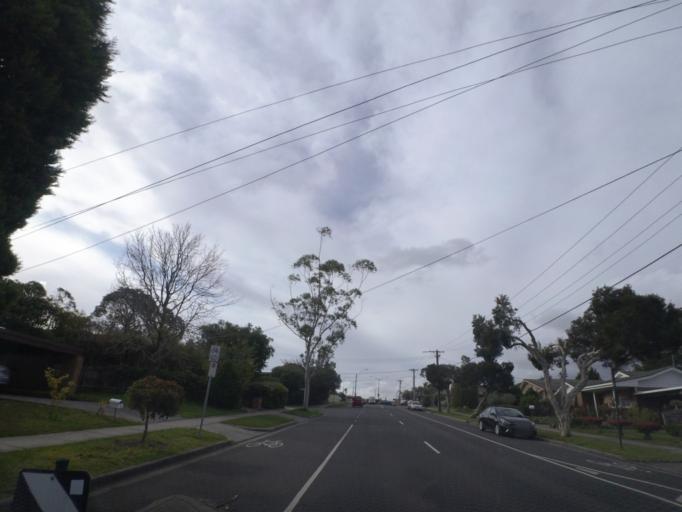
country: AU
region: Victoria
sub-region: Whitehorse
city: Vermont South
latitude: -37.8581
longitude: 145.1828
